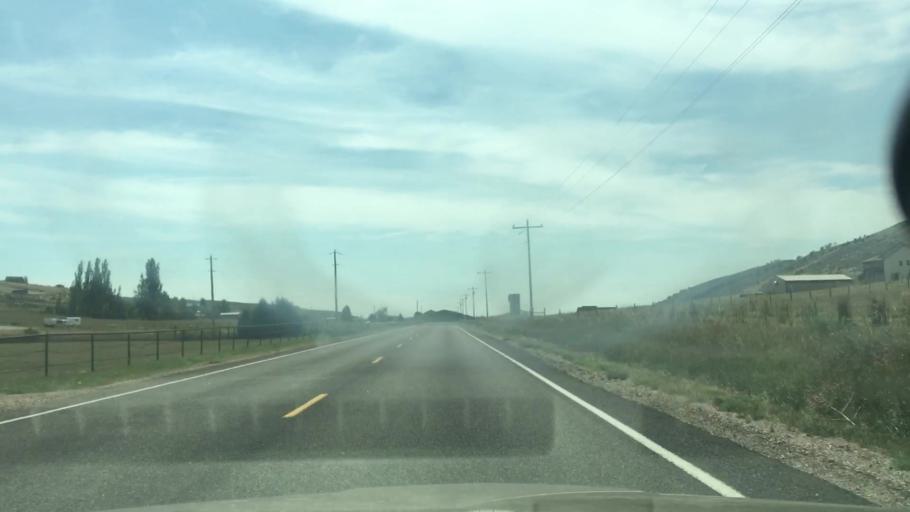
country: US
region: Colorado
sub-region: Larimer County
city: Campion
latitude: 40.3534
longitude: -105.1844
